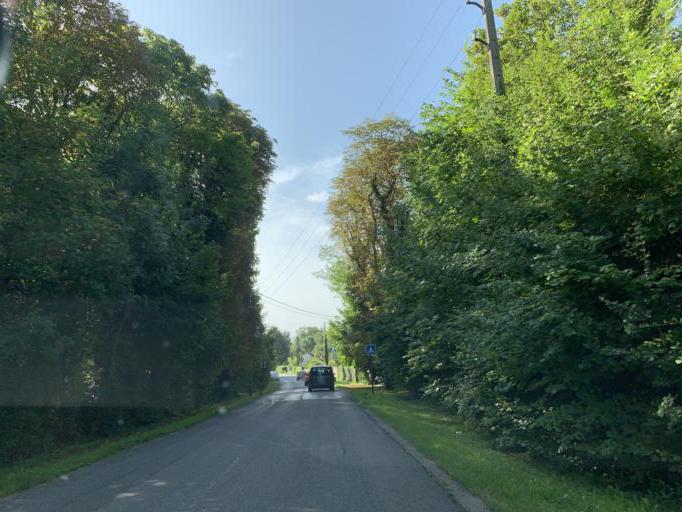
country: FR
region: Ile-de-France
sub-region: Departement de Seine-et-Marne
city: Chalifert
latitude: 48.9003
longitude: 2.7724
